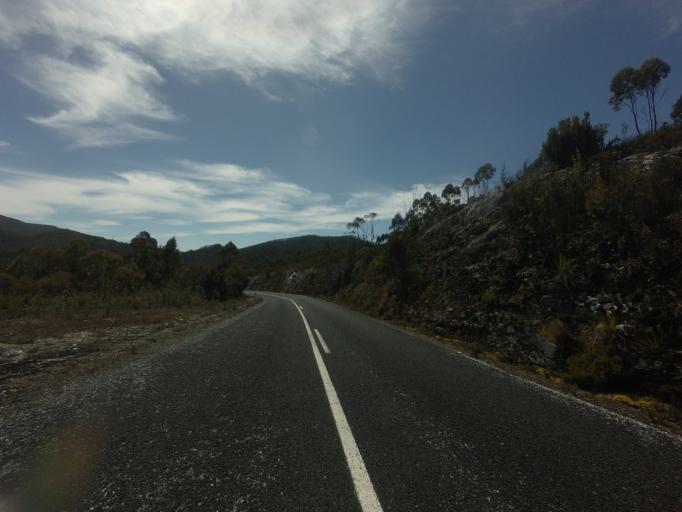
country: AU
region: Tasmania
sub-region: Huon Valley
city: Geeveston
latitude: -42.8075
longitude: 146.0973
